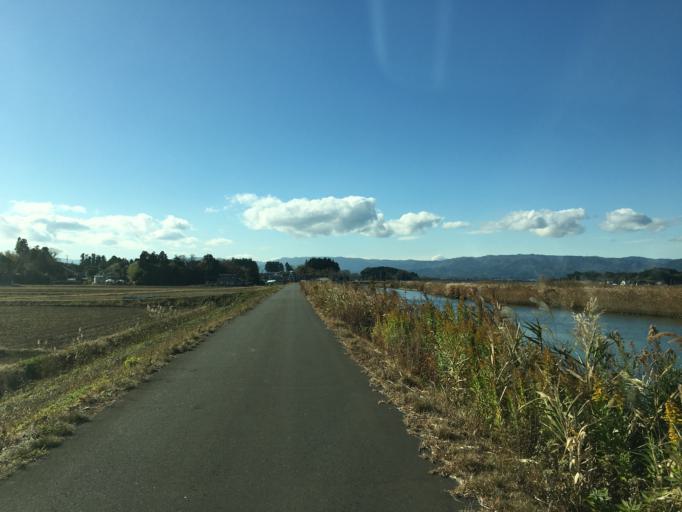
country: JP
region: Miyagi
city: Marumori
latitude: 37.8100
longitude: 140.9664
